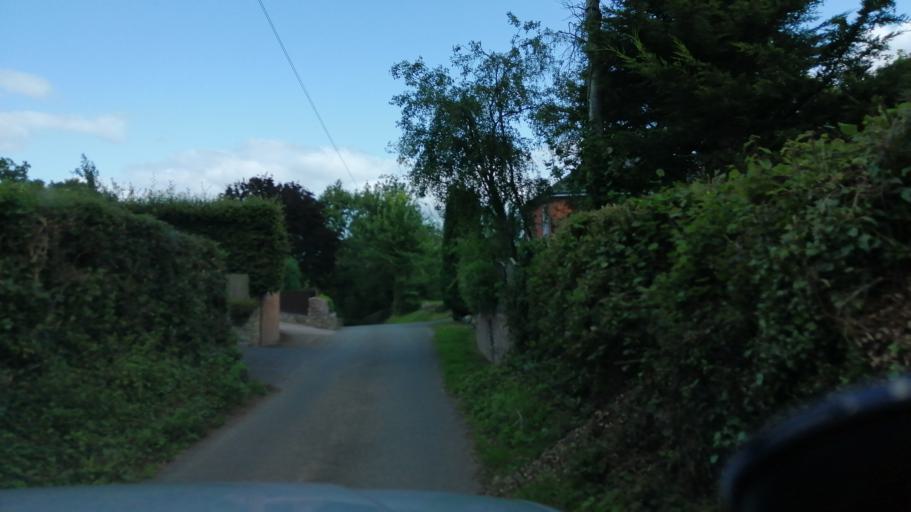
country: GB
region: England
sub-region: Herefordshire
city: Yazor
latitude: 52.1194
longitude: -2.9082
